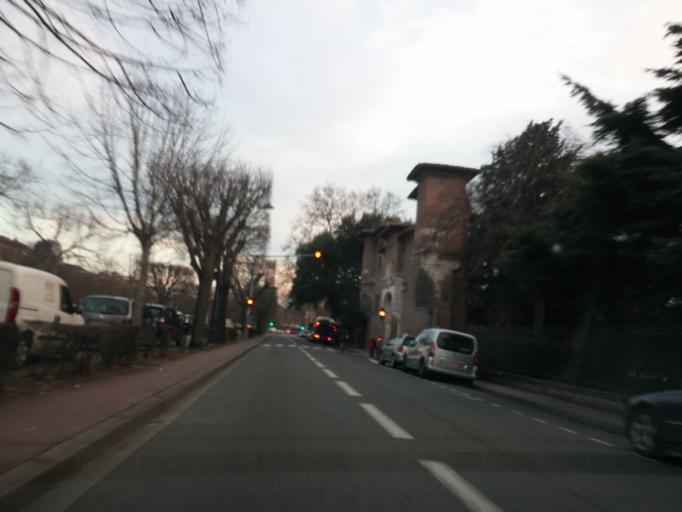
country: FR
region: Midi-Pyrenees
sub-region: Departement de la Haute-Garonne
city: Toulouse
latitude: 43.5932
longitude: 1.4526
